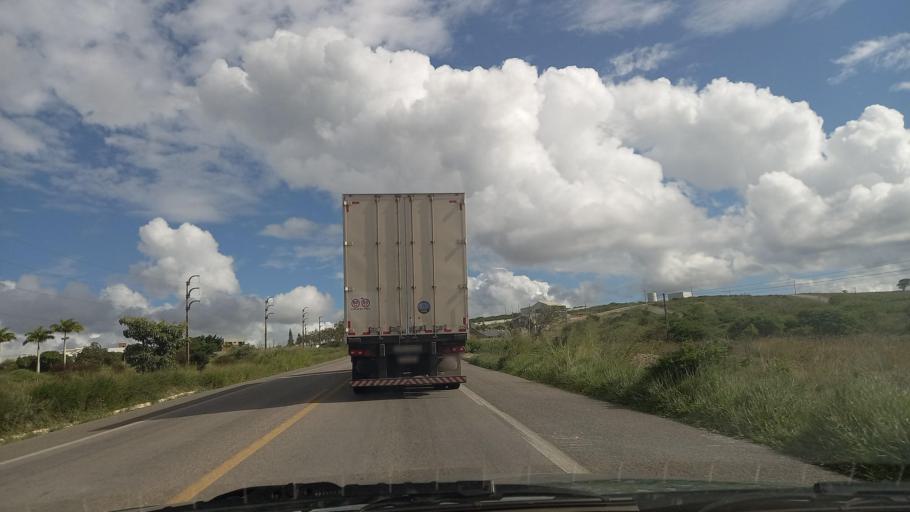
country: BR
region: Pernambuco
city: Garanhuns
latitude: -8.8556
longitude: -36.4635
